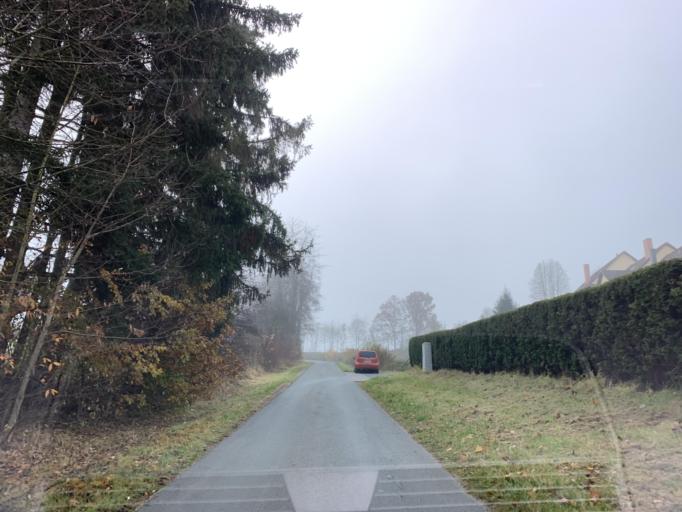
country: DE
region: Bavaria
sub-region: Upper Palatinate
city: Neunburg vorm Wald
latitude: 49.3482
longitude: 12.3990
